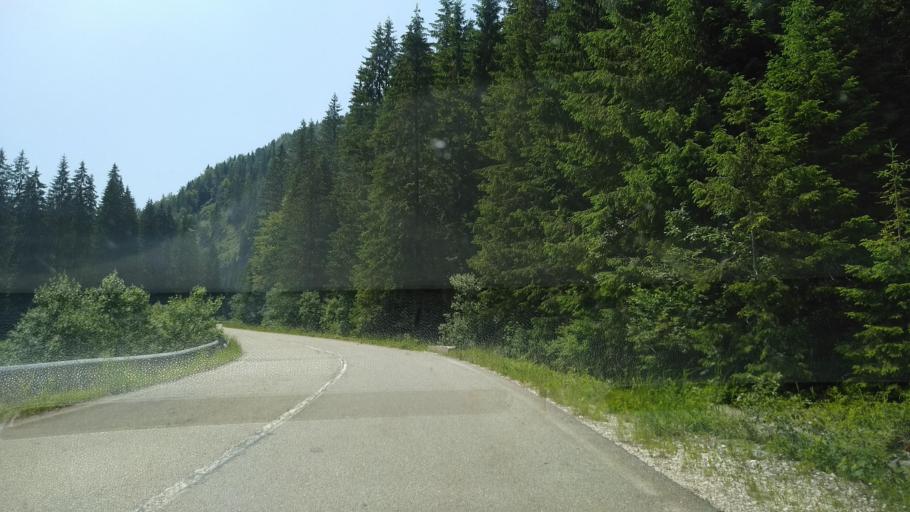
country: RO
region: Gorj
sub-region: Comuna Tismana
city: Sohodol
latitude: 45.2683
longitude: 22.8842
